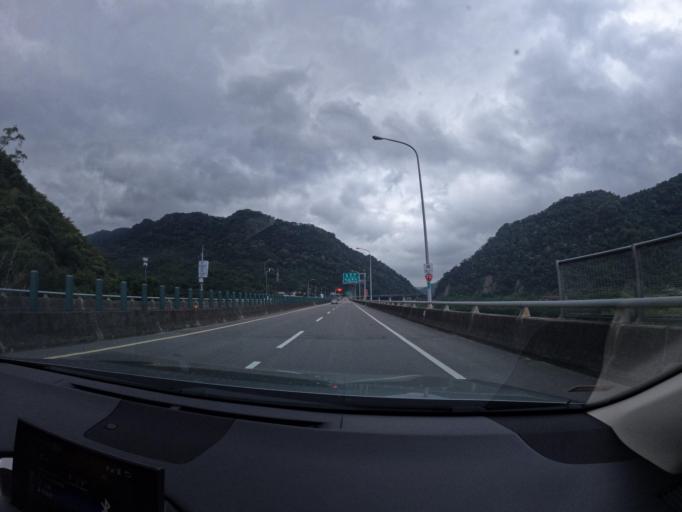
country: TW
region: Taiwan
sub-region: Miaoli
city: Miaoli
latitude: 24.4606
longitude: 120.8626
